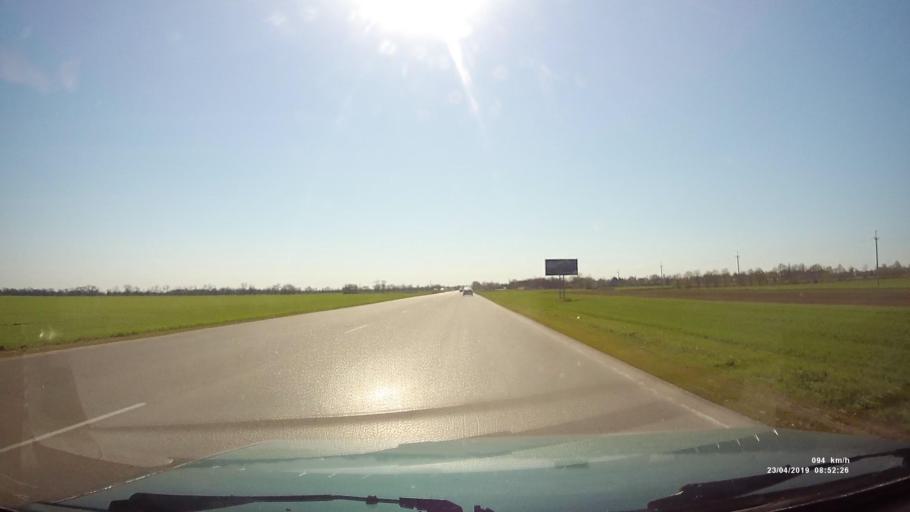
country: RU
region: Rostov
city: Sal'sk
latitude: 46.4814
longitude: 41.4595
